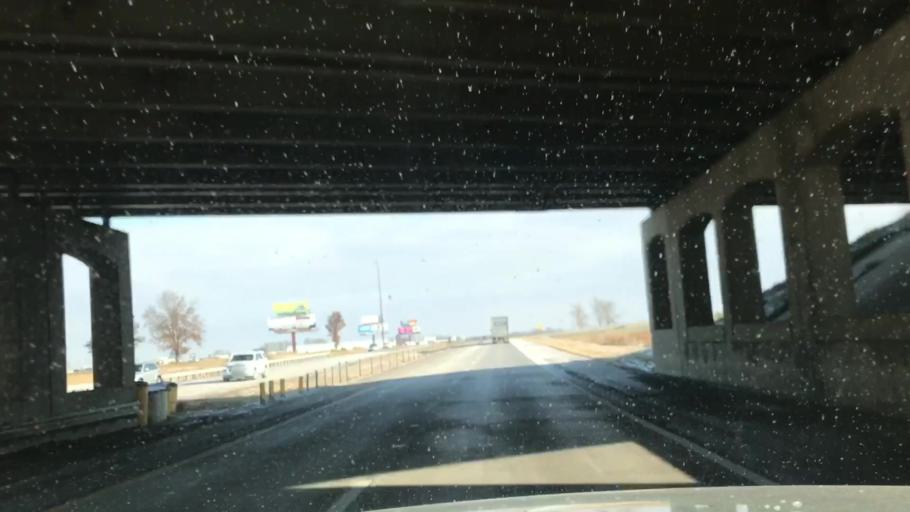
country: US
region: Illinois
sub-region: Madison County
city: Worden
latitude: 38.8891
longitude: -89.8376
